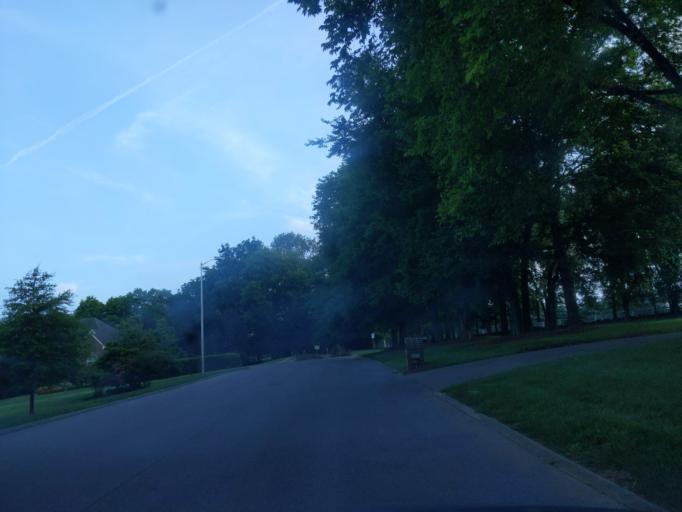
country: US
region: Tennessee
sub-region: Williamson County
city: Brentwood Estates
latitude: 36.0105
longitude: -86.7712
